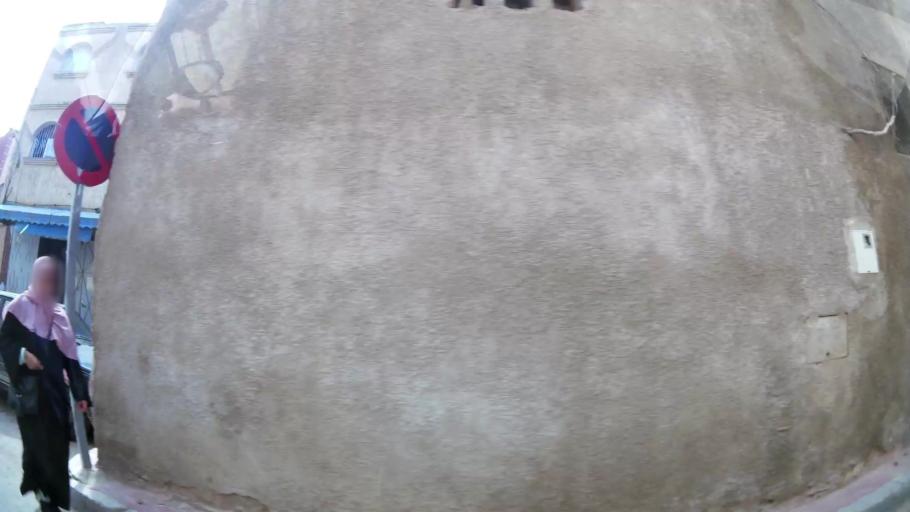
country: MA
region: Oriental
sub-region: Oujda-Angad
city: Oujda
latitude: 34.6821
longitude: -1.9071
